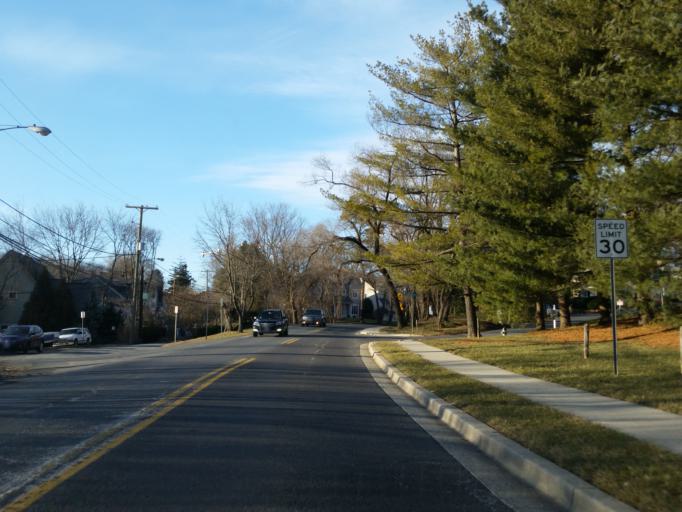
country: US
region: Maryland
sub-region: Montgomery County
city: Brookmont
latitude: 38.9451
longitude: -77.1174
